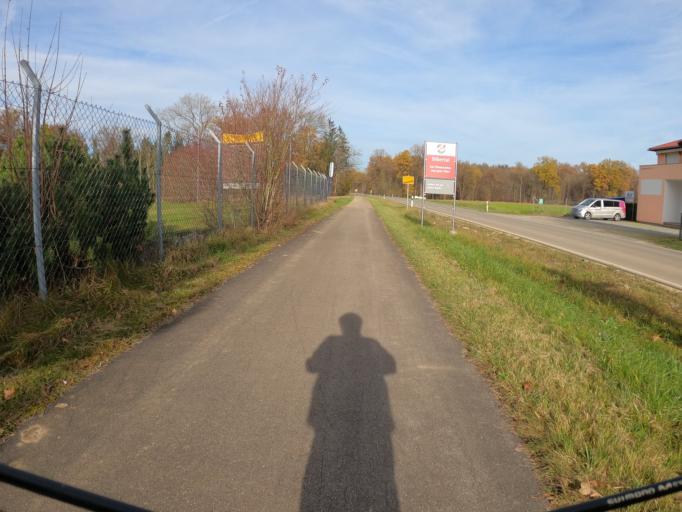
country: DE
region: Bavaria
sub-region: Swabia
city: Leipheim
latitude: 48.4326
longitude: 10.1897
